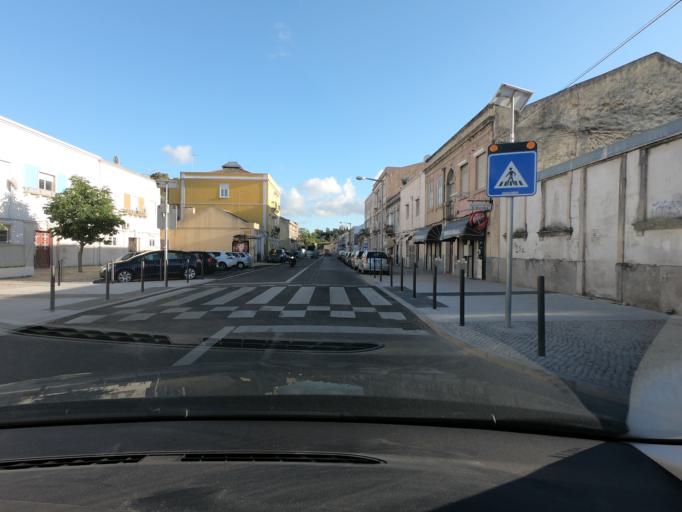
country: PT
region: Lisbon
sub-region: Lisbon
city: Lisbon
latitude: 38.7360
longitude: -9.1171
